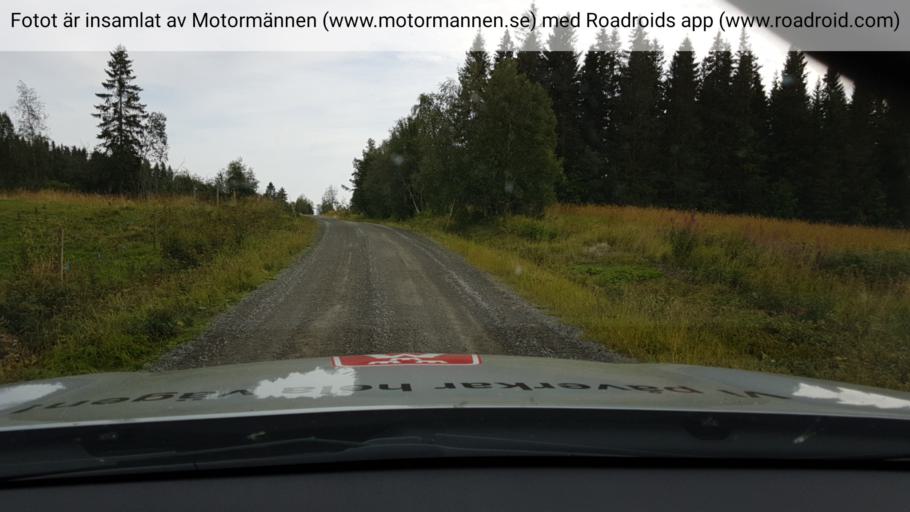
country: SE
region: Jaemtland
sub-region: Krokoms Kommun
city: Valla
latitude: 63.5245
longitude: 13.8868
